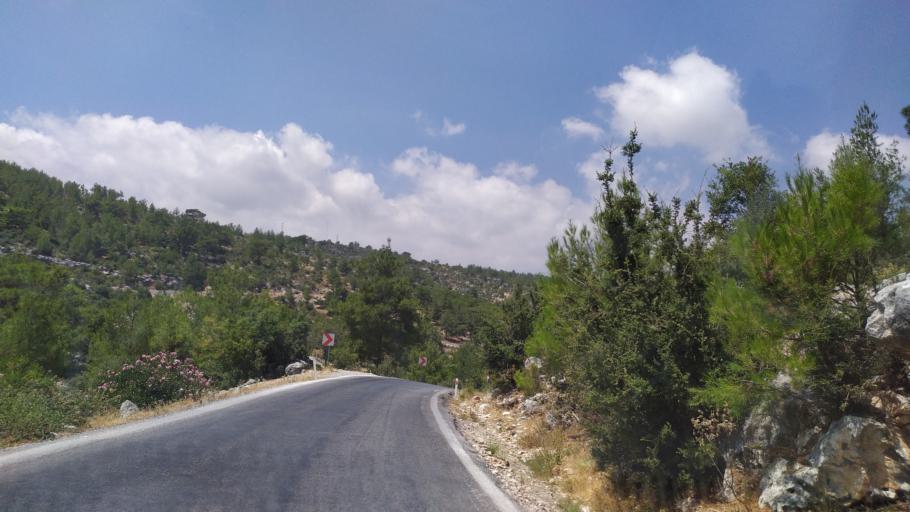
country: TR
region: Mersin
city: Gulnar
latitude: 36.2752
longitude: 33.3843
